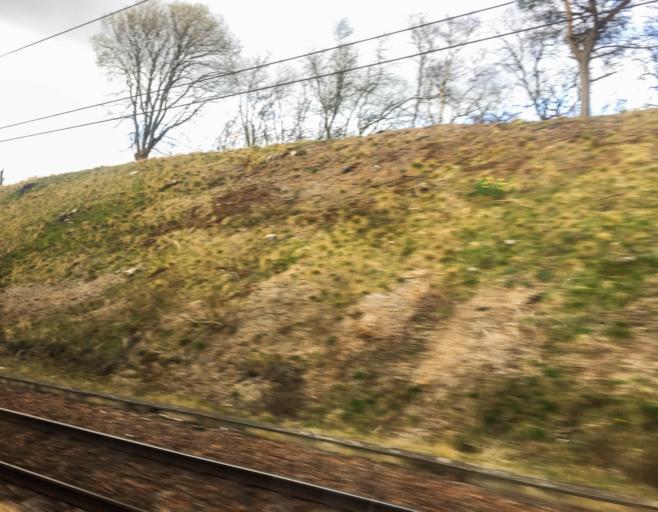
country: GB
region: Scotland
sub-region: South Lanarkshire
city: Law
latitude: 55.7569
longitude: -3.8791
